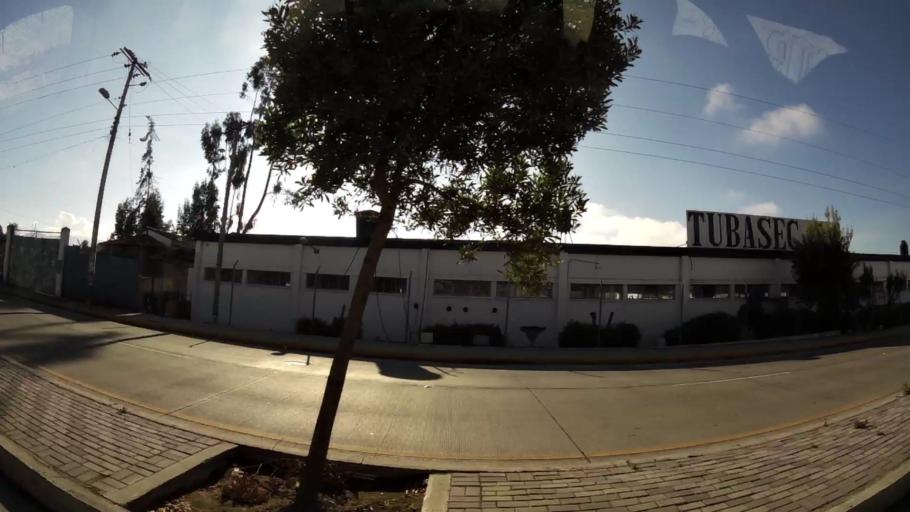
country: EC
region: Chimborazo
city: Riobamba
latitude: -1.6886
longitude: -78.6312
